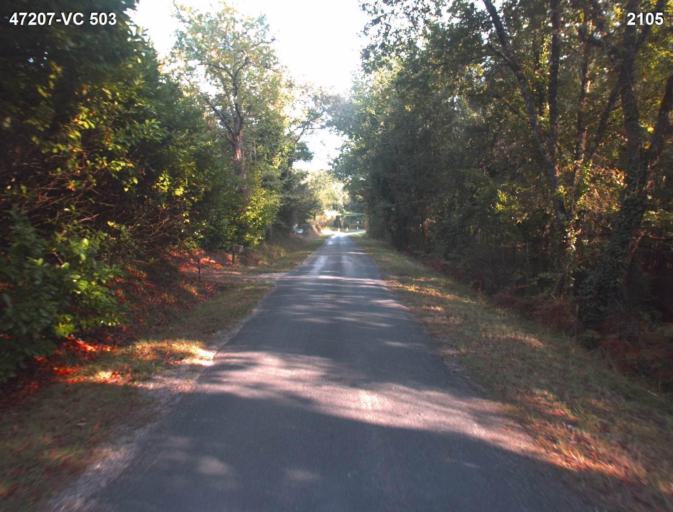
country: FR
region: Aquitaine
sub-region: Departement du Lot-et-Garonne
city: Barbaste
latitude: 44.1895
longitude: 0.2322
